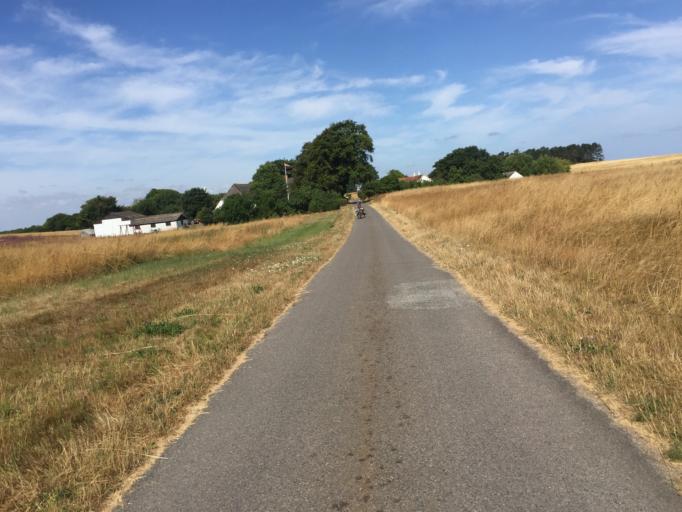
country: DK
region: Central Jutland
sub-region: Samso Kommune
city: Tranebjerg
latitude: 55.9549
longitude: 10.4220
